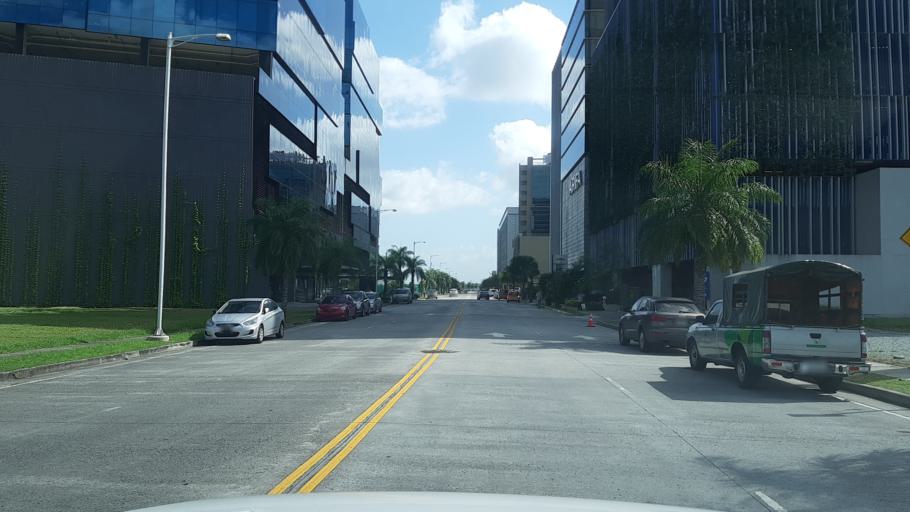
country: PA
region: Panama
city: San Miguelito
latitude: 9.0280
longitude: -79.4630
